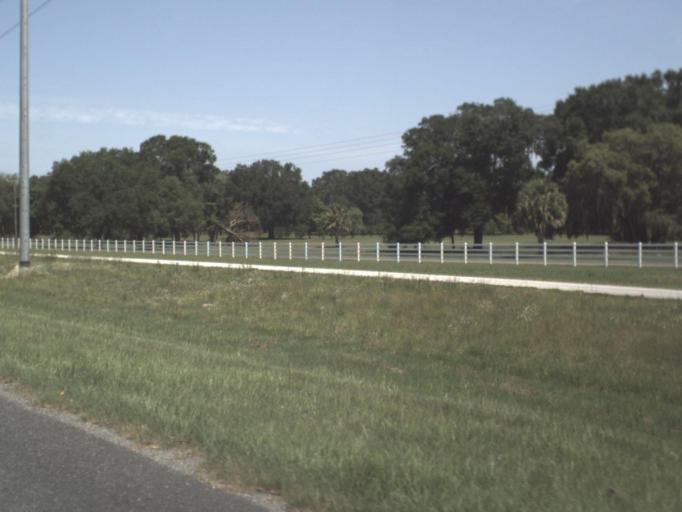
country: US
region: Florida
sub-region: Dixie County
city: Cross City
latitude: 29.6047
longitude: -83.0342
